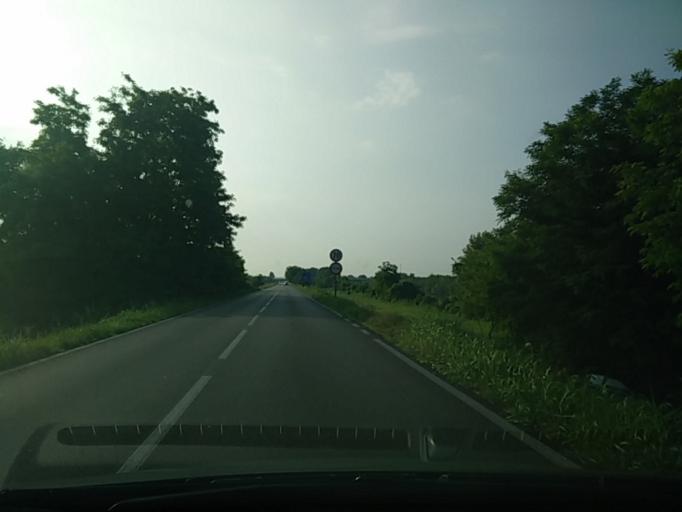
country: IT
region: Veneto
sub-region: Provincia di Venezia
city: Passarella
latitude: 45.6112
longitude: 12.5868
